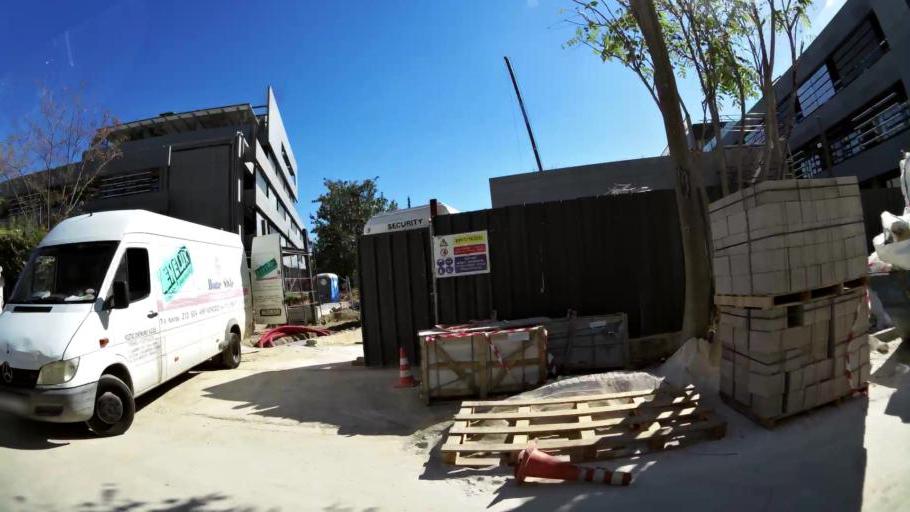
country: GR
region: Attica
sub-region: Nomarchia Athinas
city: Khalandrion
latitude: 38.0366
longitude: 23.8012
